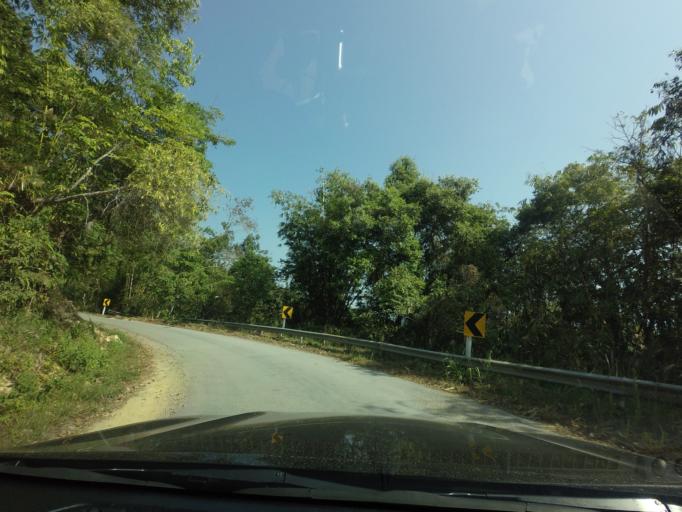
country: TH
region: Kanchanaburi
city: Thong Pha Phum
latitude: 14.6995
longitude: 98.4588
